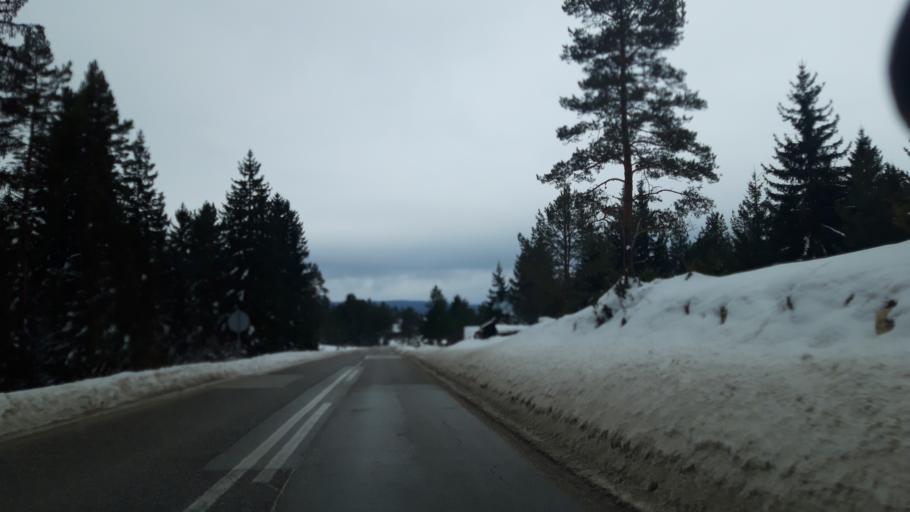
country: BA
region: Republika Srpska
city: Han Pijesak
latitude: 44.0422
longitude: 18.9307
